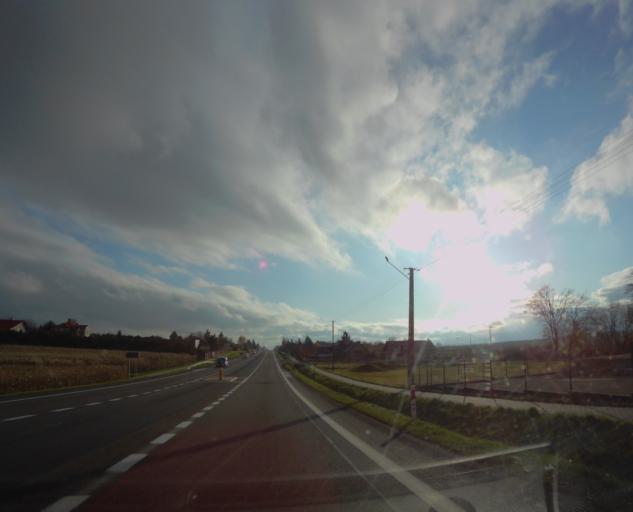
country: PL
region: Subcarpathian Voivodeship
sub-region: Powiat przemyski
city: Orly
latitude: 49.8685
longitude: 22.8100
